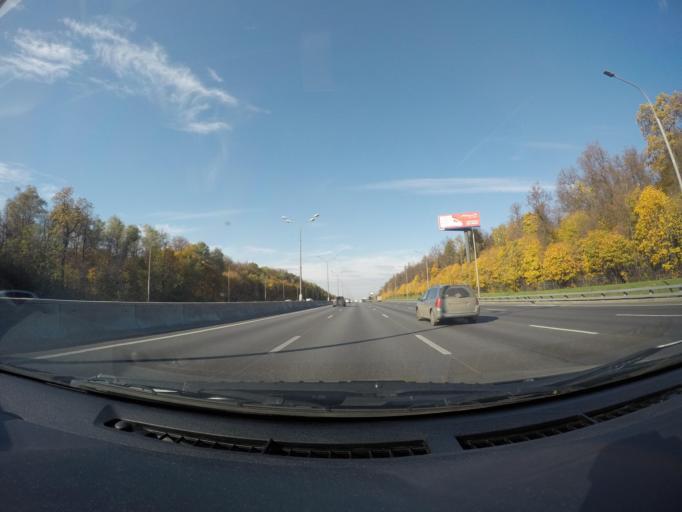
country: RU
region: Moscow
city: Gol'yanovo
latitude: 55.8368
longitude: 37.8148
